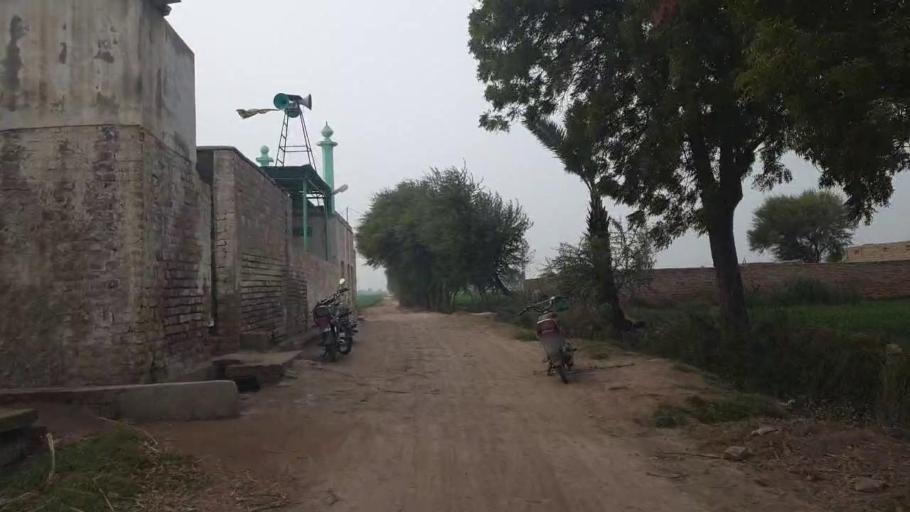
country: PK
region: Sindh
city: Shahdadpur
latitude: 25.8724
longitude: 68.6268
